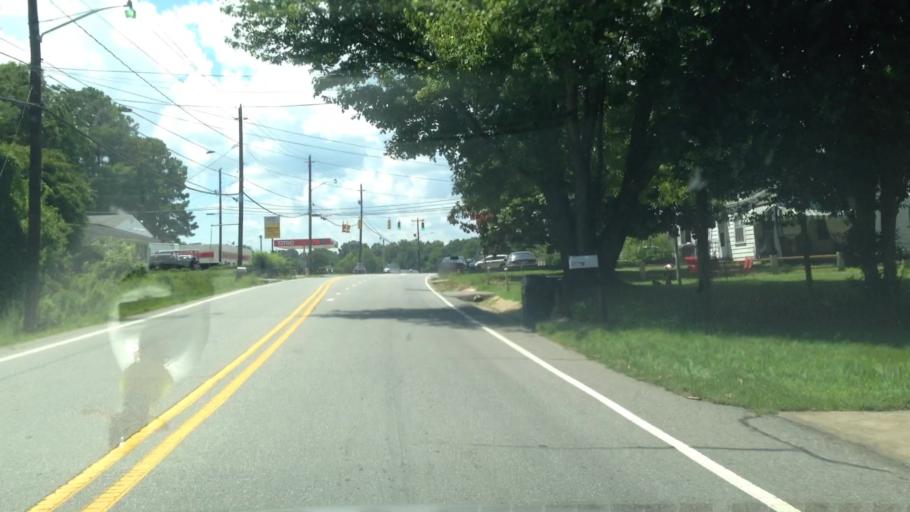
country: US
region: North Carolina
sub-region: Rockingham County
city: Reidsville
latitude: 36.3551
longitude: -79.6767
